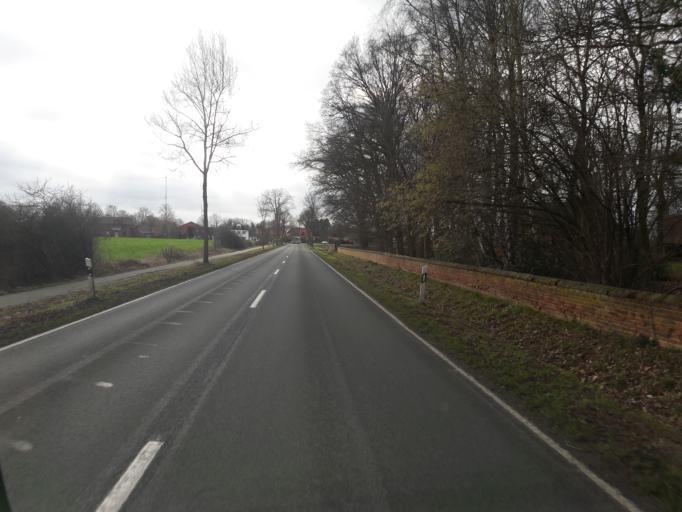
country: DE
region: Lower Saxony
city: Warmsen
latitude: 52.4602
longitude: 8.8532
